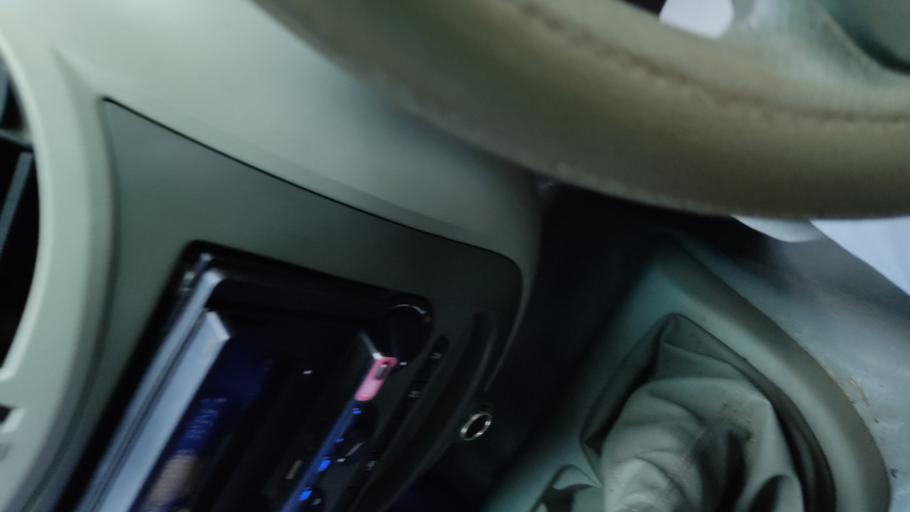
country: IN
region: Kerala
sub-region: Pattanamtitta
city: Tiruvalla
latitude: 9.3316
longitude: 76.5248
